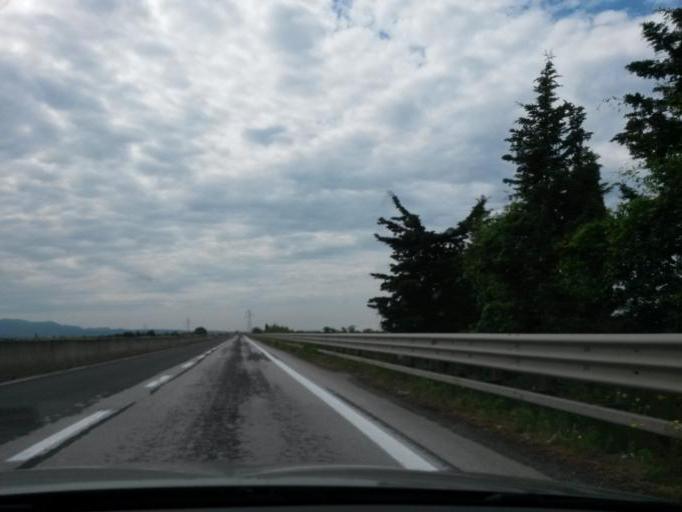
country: IT
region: Tuscany
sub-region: Provincia di Livorno
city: La California
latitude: 43.2380
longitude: 10.5560
